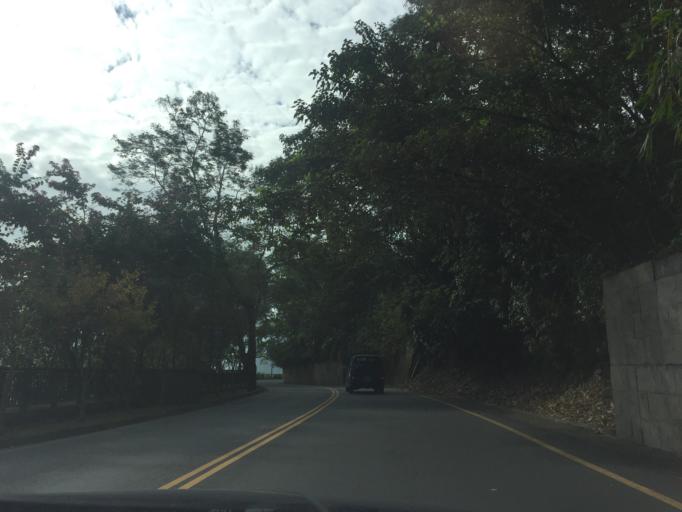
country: TW
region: Taiwan
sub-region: Nantou
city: Puli
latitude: 23.8638
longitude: 120.9040
